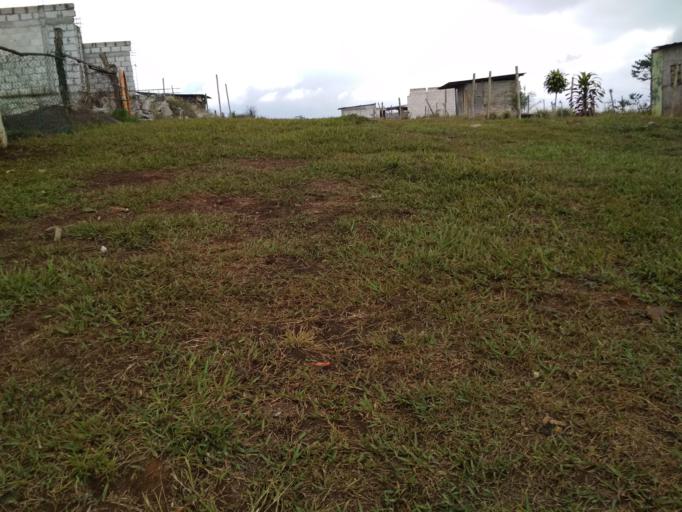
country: MX
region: Veracruz
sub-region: Cordoba
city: San Jose de Tapia
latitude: 18.8471
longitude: -96.9650
